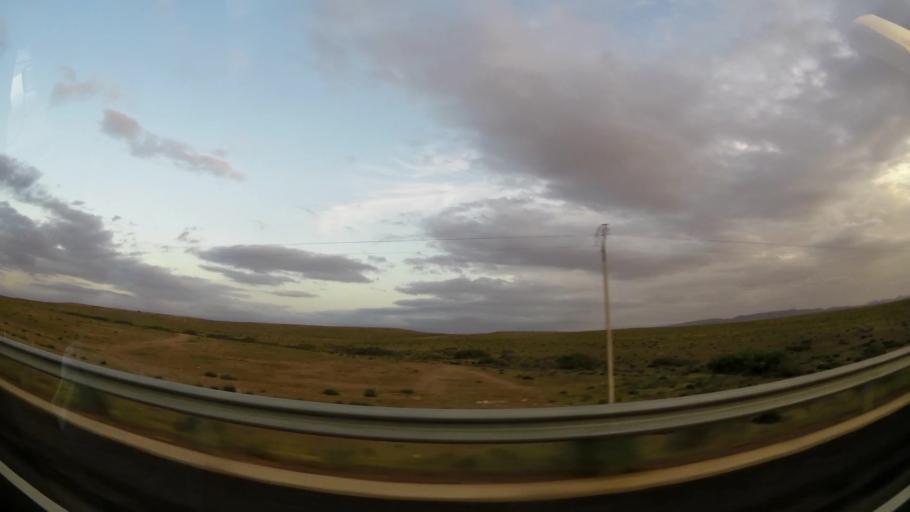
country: MA
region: Oriental
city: Taourirt
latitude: 34.5492
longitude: -2.8830
